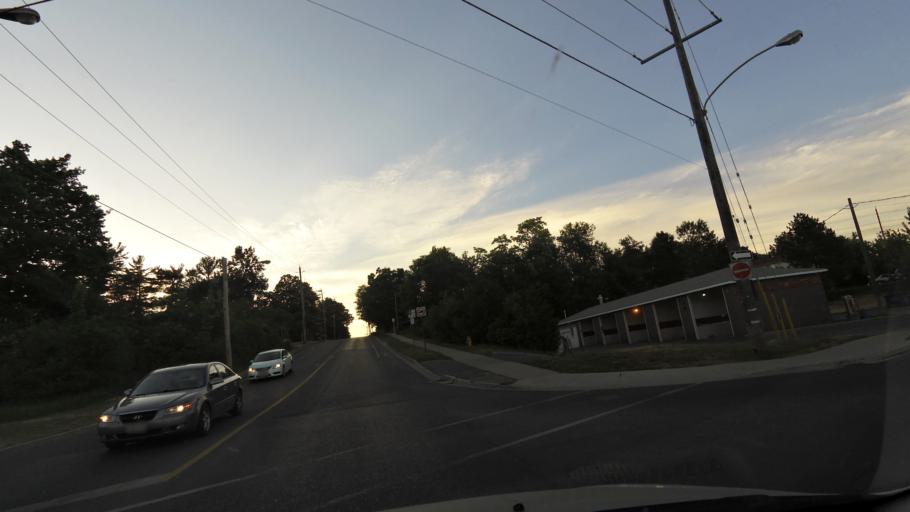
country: CA
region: Ontario
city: Peterborough
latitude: 44.3219
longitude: -78.3168
